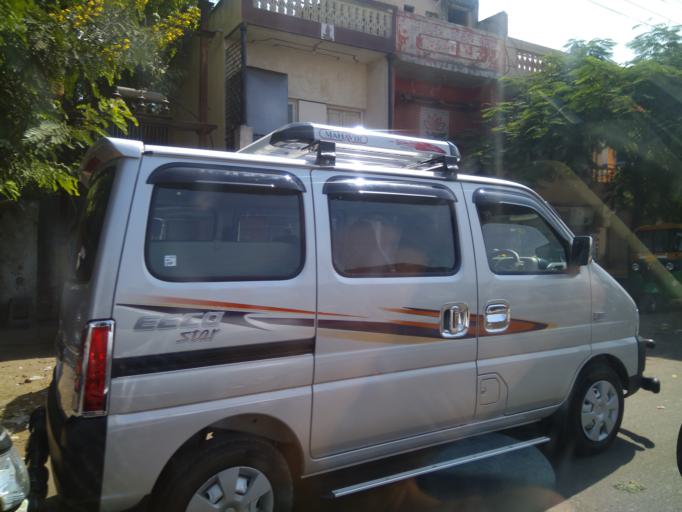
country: IN
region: Gujarat
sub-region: Jamnagar
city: Jamnagar
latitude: 22.4554
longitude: 70.0683
